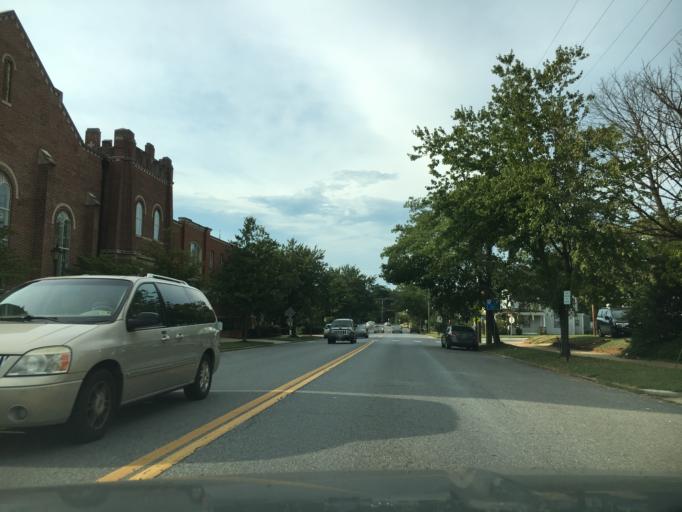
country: US
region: Virginia
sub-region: City of Lynchburg
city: Lynchburg
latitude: 37.4288
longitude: -79.1539
